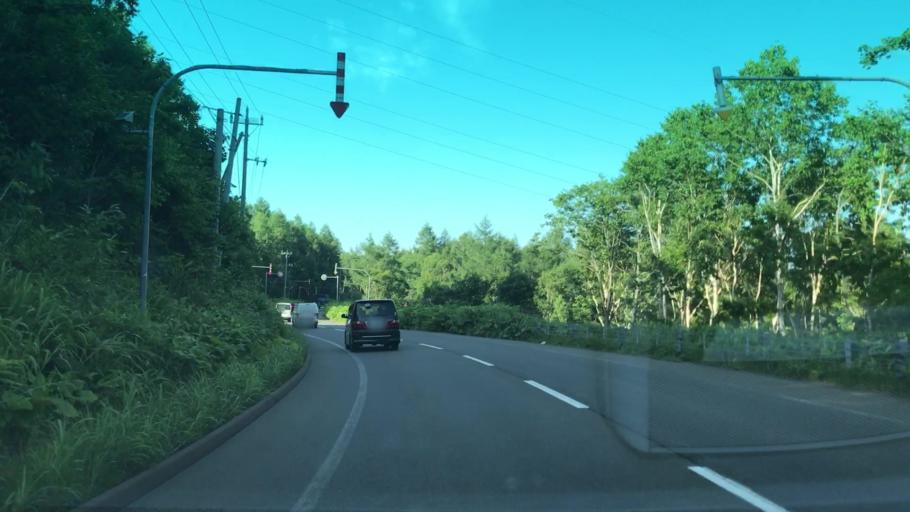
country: JP
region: Hokkaido
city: Otaru
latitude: 43.1108
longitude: 141.0077
